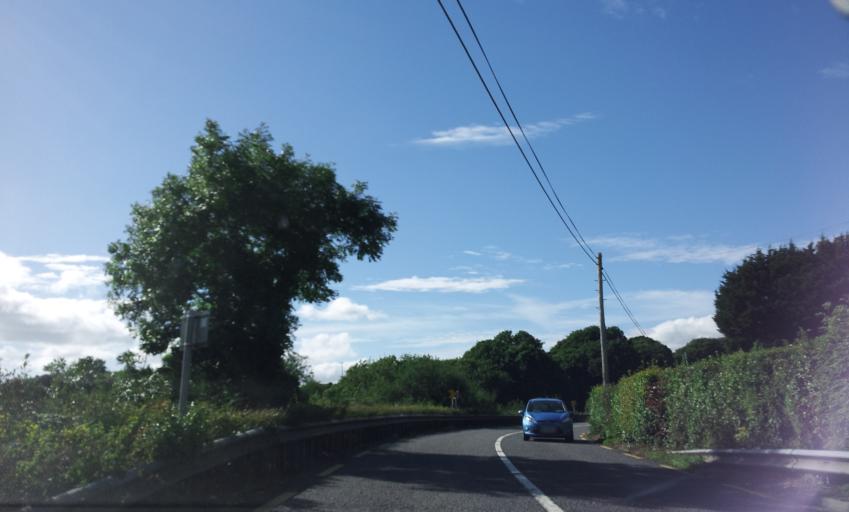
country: IE
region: Munster
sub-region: County Cork
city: Macroom
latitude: 51.9190
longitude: -9.0853
